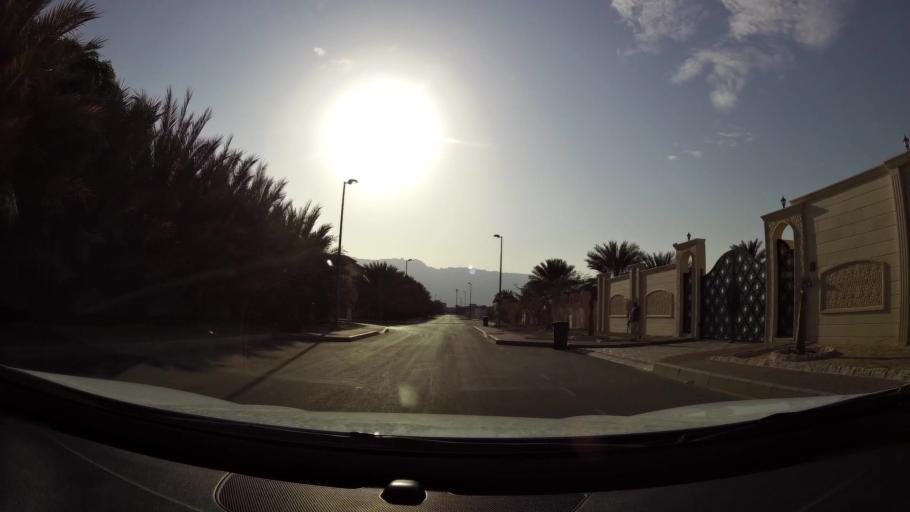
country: AE
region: Abu Dhabi
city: Al Ain
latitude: 24.0781
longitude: 55.8472
